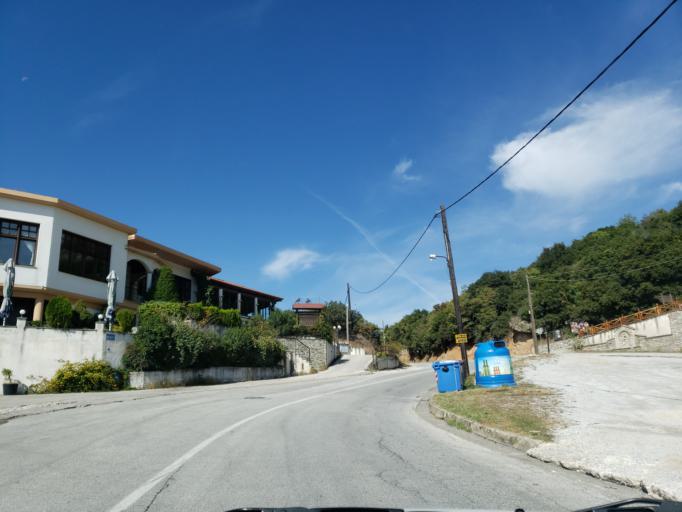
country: GR
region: Thessaly
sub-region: Trikala
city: Kastraki
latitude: 39.7090
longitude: 21.6180
